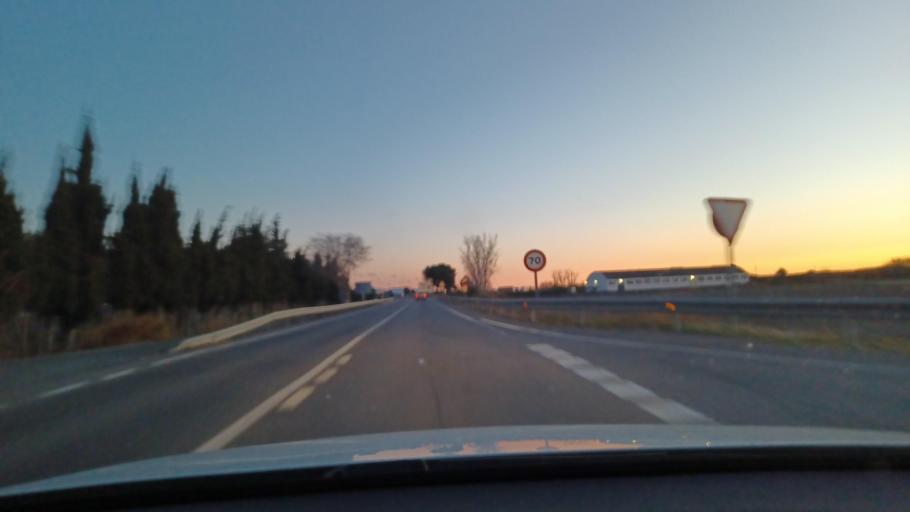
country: ES
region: Catalonia
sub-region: Provincia de Tarragona
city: Amposta
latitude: 40.7192
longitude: 0.5862
